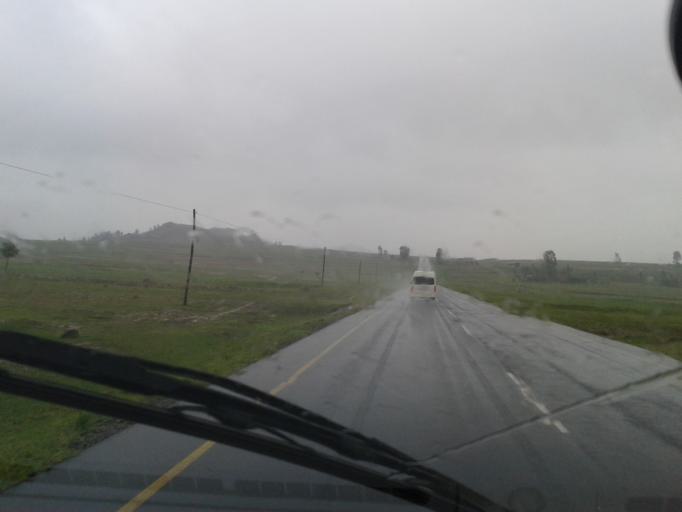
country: LS
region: Mafeteng
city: Mafeteng
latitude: -29.6724
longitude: 27.4499
